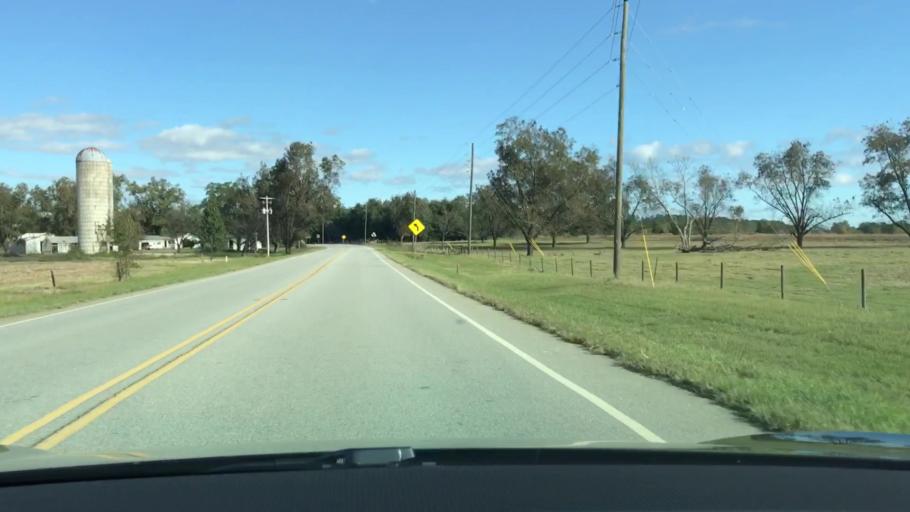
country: US
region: Georgia
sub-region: Jefferson County
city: Wrens
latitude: 33.1533
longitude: -82.4567
